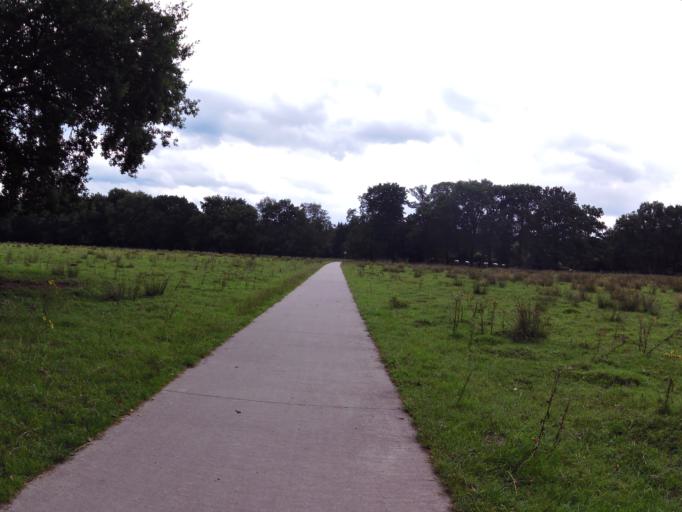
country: NL
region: Gelderland
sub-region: Gemeente Rheden
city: De Steeg
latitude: 52.0436
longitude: 6.0536
